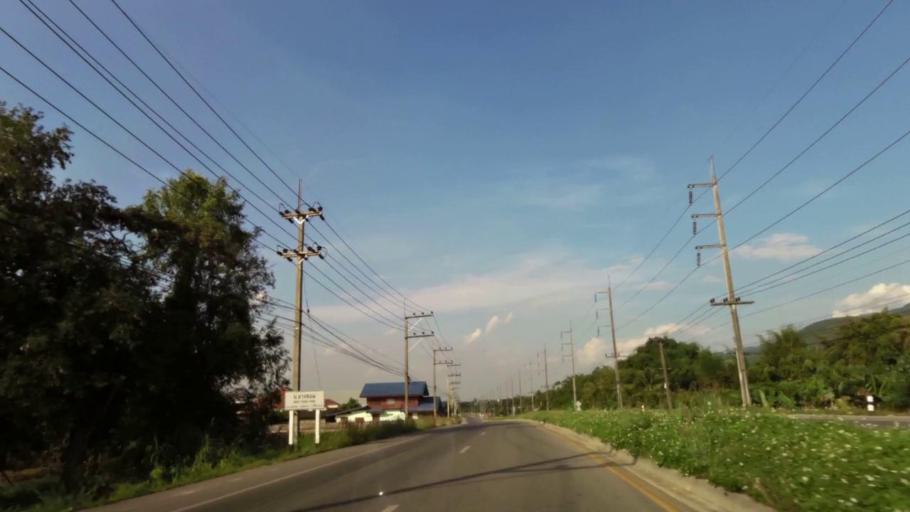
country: TH
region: Chiang Rai
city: Khun Tan
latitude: 19.8994
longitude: 100.2955
